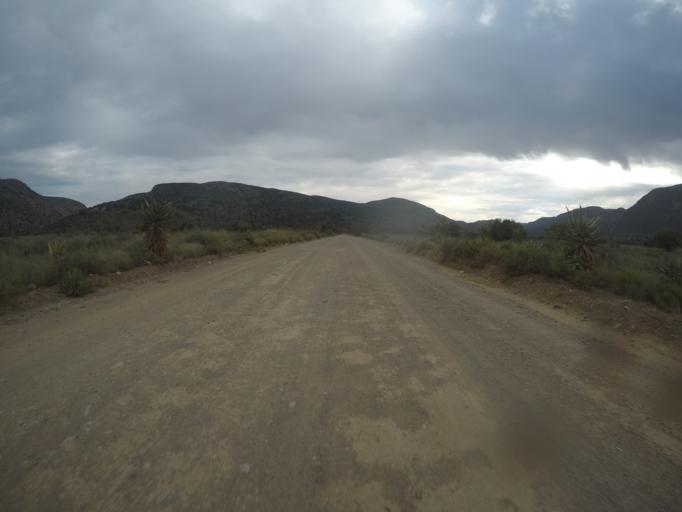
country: ZA
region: Eastern Cape
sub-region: Cacadu District Municipality
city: Willowmore
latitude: -33.5267
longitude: 23.8645
